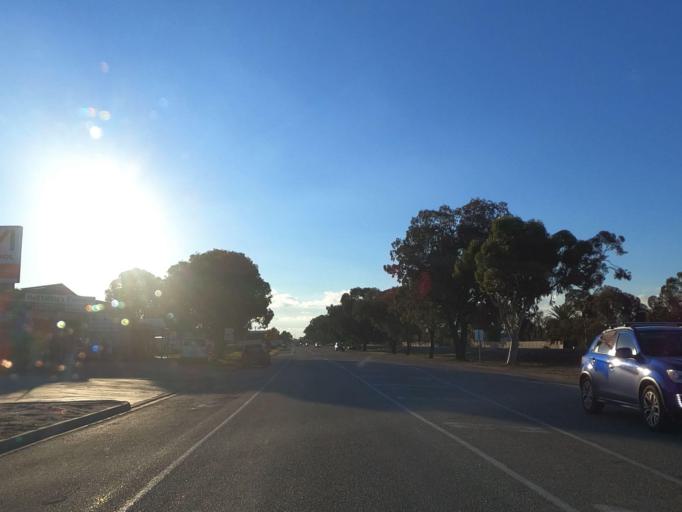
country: AU
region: Victoria
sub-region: Swan Hill
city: Swan Hill
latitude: -35.3325
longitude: 143.5582
